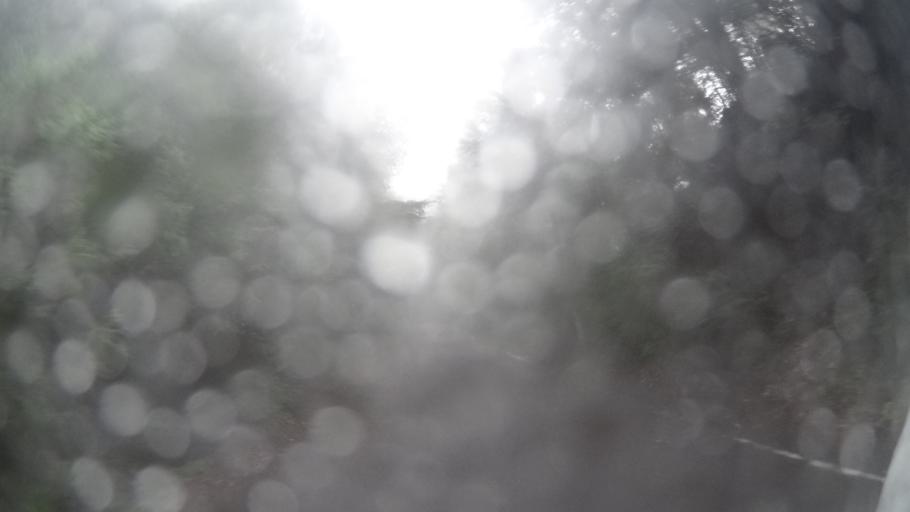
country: JP
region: Kagoshima
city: Nishinoomote
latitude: 30.3033
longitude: 130.5521
